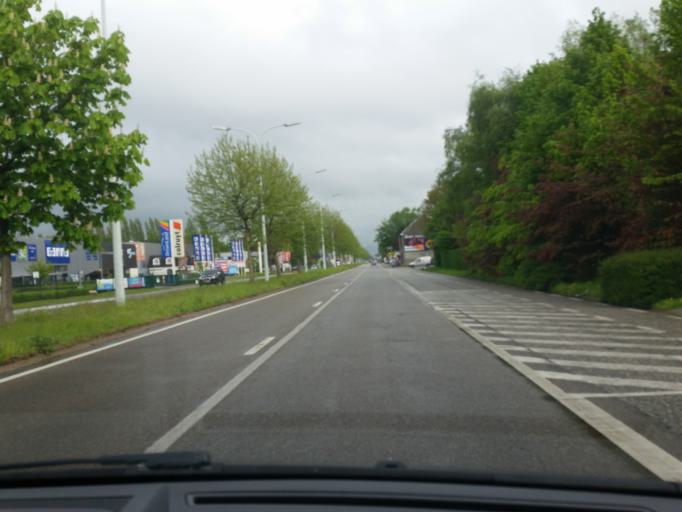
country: BE
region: Flanders
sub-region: Provincie Antwerpen
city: Lier
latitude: 51.1461
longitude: 4.5409
